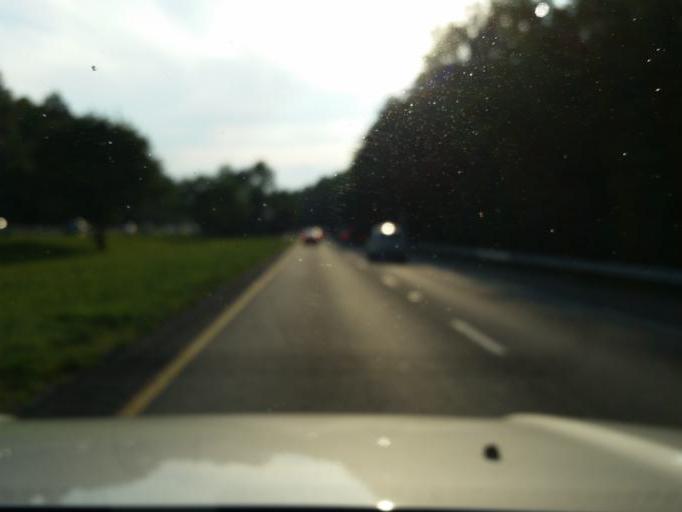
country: US
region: Virginia
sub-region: Henrico County
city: Sandston
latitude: 37.5177
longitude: -77.2002
